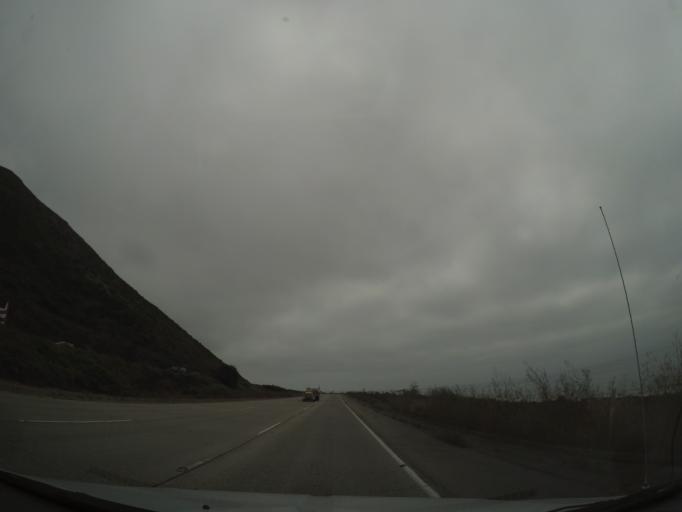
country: US
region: California
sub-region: Ventura County
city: Ventura
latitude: 34.3250
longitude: -119.3940
